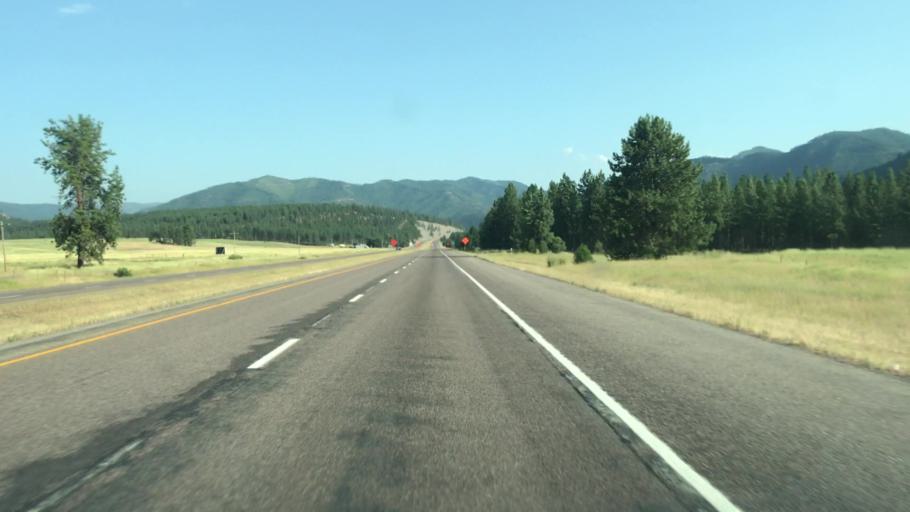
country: US
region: Montana
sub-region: Mineral County
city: Superior
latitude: 47.0384
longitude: -114.7479
